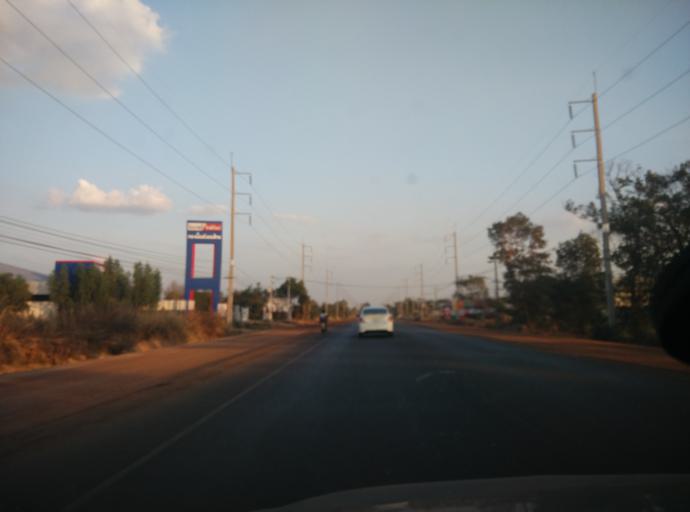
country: TH
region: Sisaket
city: Si Sa Ket
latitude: 15.1405
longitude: 104.2598
